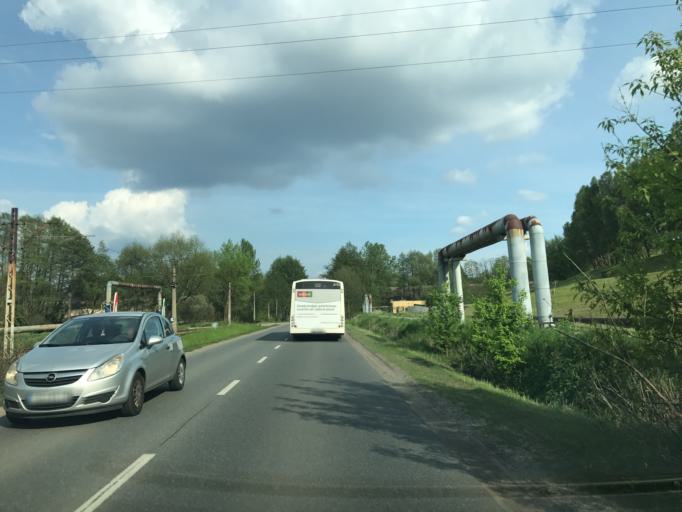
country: PL
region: Kujawsko-Pomorskie
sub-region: Powiat bydgoski
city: Osielsko
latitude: 53.1165
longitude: 18.0959
